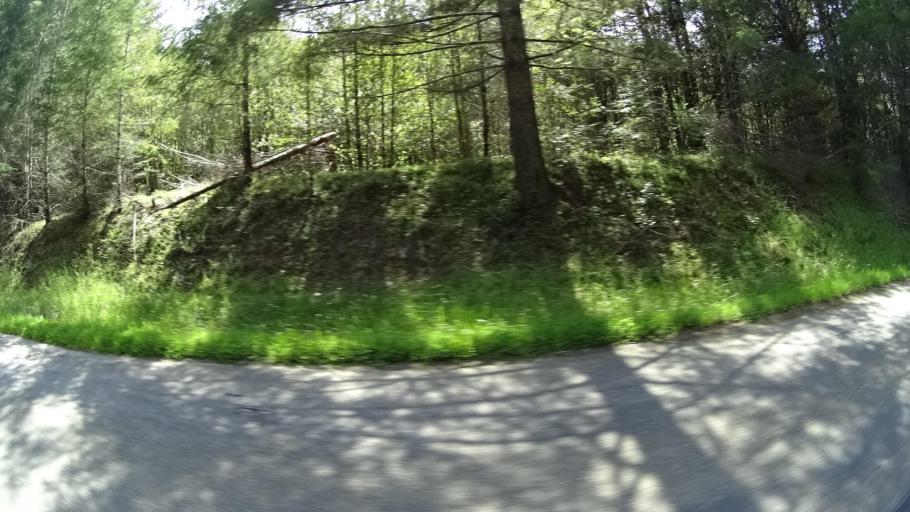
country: US
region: California
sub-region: Humboldt County
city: Rio Dell
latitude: 40.4452
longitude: -123.7951
